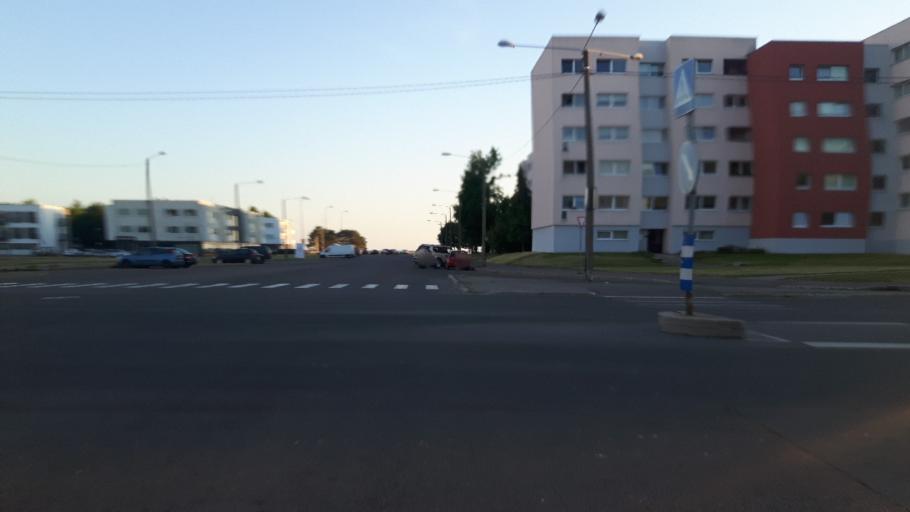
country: EE
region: Paernumaa
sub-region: Paernu linn
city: Parnu
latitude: 58.3677
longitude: 24.5433
